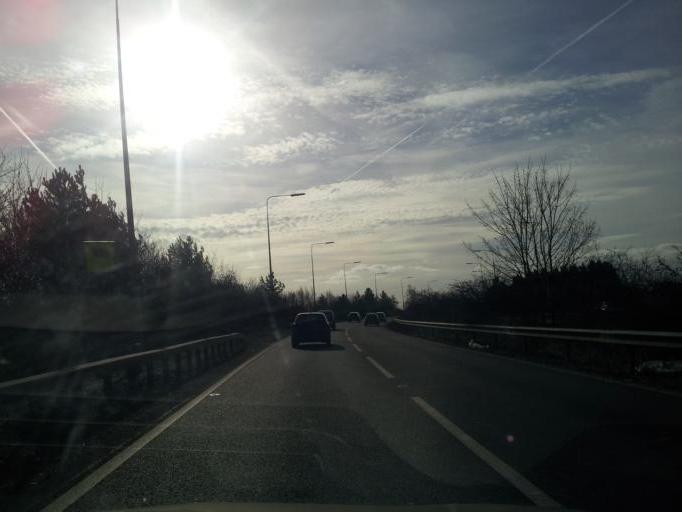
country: GB
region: England
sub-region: Central Bedfordshire
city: Biggleswade
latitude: 52.1053
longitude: -0.2782
